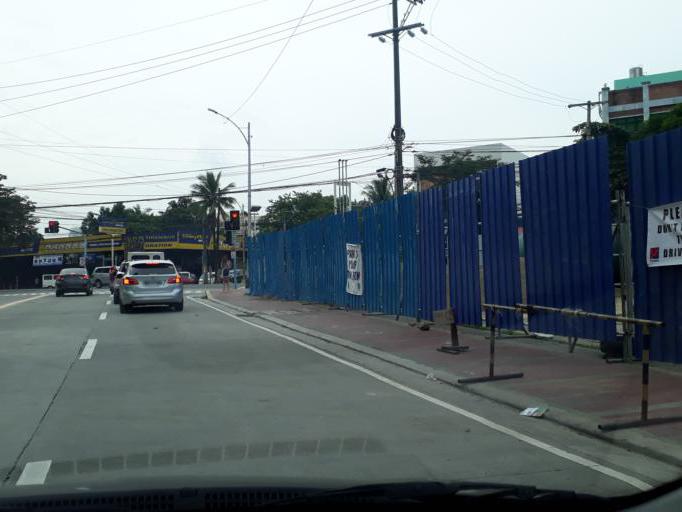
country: PH
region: Metro Manila
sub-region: Quezon City
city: Quezon City
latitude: 14.6340
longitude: 121.0412
